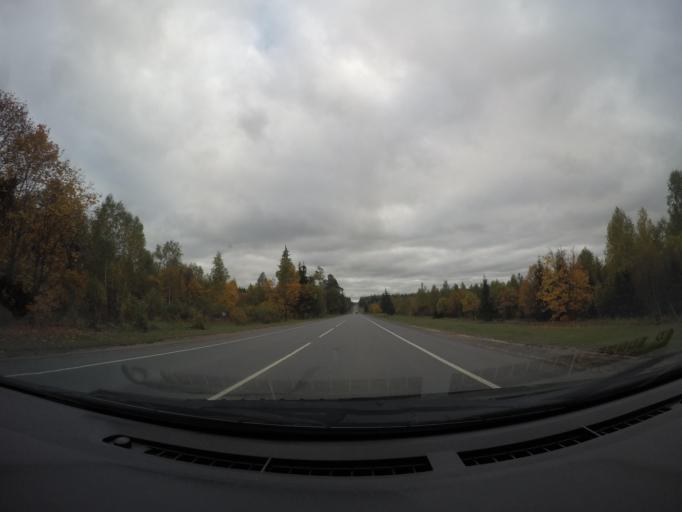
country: RU
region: Moskovskaya
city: Dorokhovo
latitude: 55.6197
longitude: 36.3449
